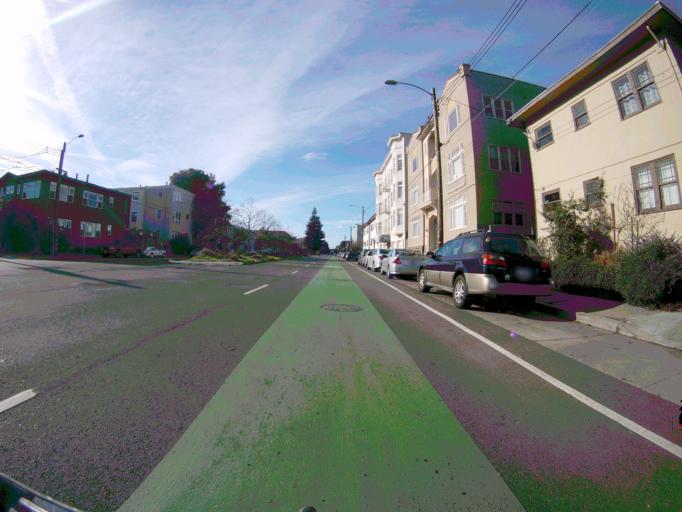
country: US
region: California
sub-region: Alameda County
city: Emeryville
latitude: 37.8288
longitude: -122.2621
